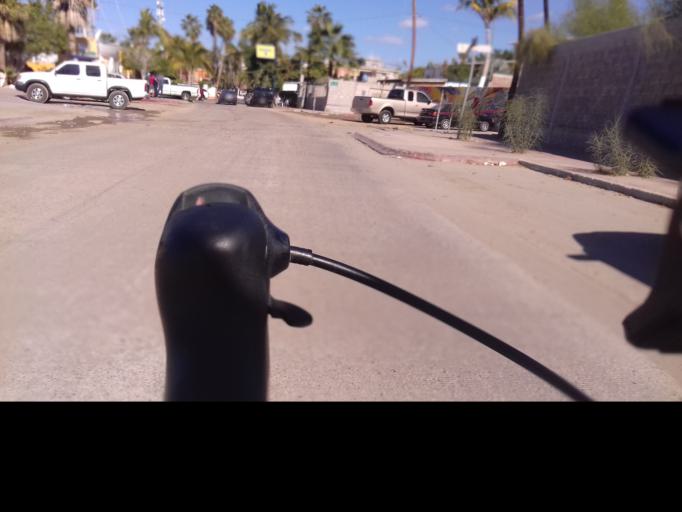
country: MX
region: Baja California Sur
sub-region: La Paz
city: La Paz
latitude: 24.1520
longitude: -110.3283
